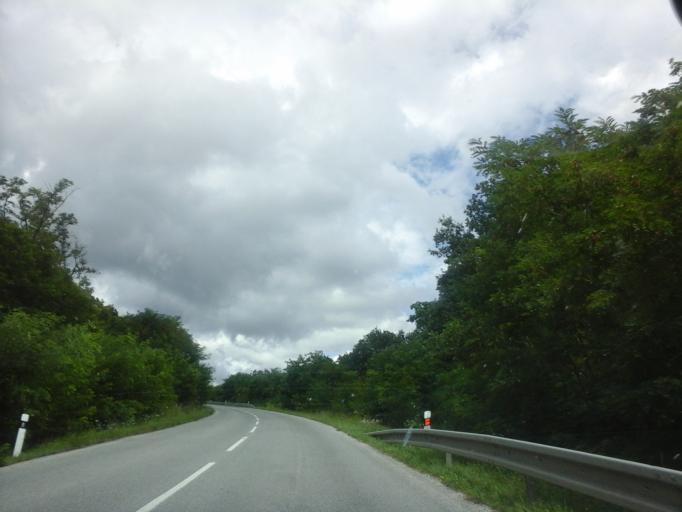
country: SK
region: Kosicky
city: Roznava
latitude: 48.5302
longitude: 20.4101
